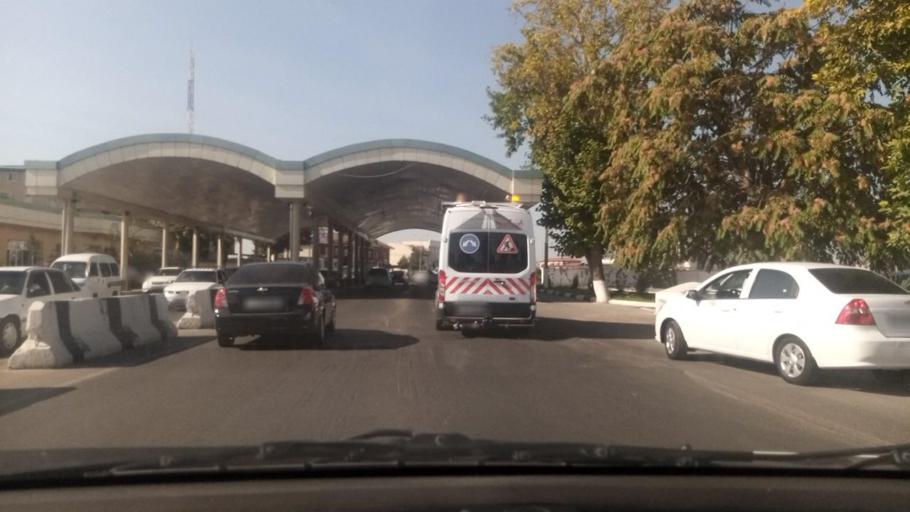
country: UZ
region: Toshkent Shahri
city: Bektemir
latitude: 41.2265
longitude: 69.3355
